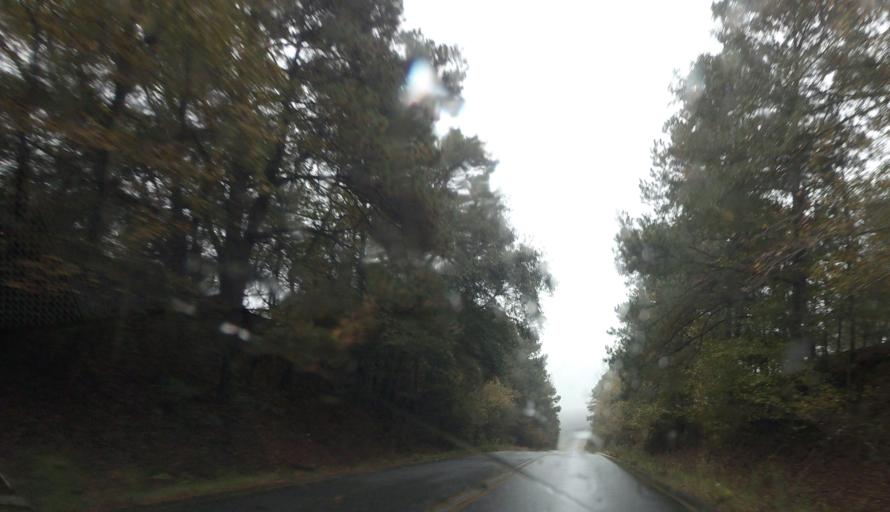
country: US
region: Georgia
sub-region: Marion County
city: Buena Vista
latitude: 32.3359
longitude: -84.5018
